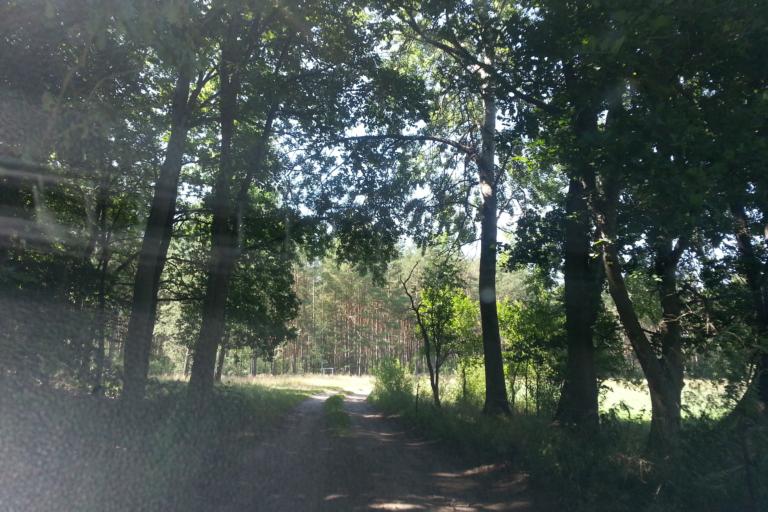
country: DE
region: Mecklenburg-Vorpommern
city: Torgelow
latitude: 53.6594
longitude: 14.0350
